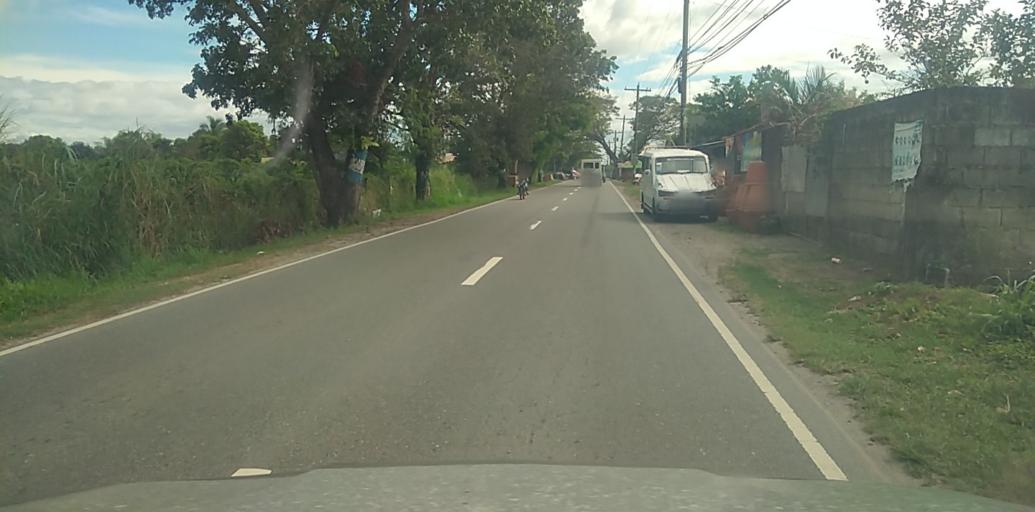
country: PH
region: Central Luzon
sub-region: Province of Pampanga
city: Arenas
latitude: 15.1785
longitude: 120.6783
